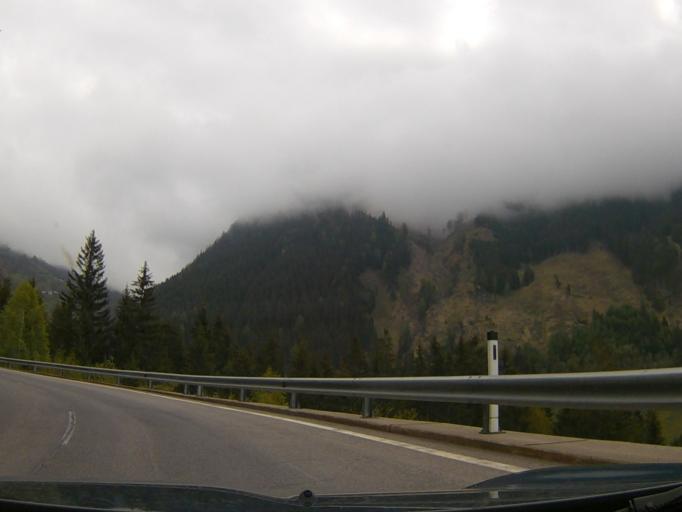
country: AT
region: Carinthia
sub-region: Politischer Bezirk Spittal an der Drau
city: Obervellach
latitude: 46.9672
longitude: 13.1842
